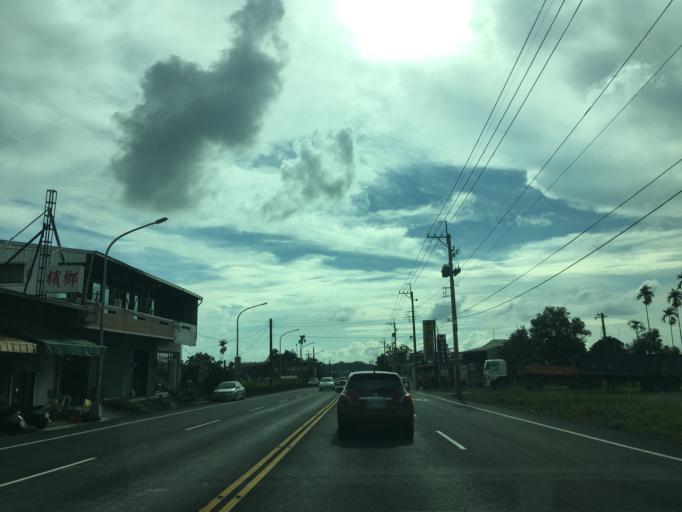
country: TW
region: Taiwan
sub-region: Chiayi
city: Jiayi Shi
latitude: 23.4420
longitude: 120.5224
